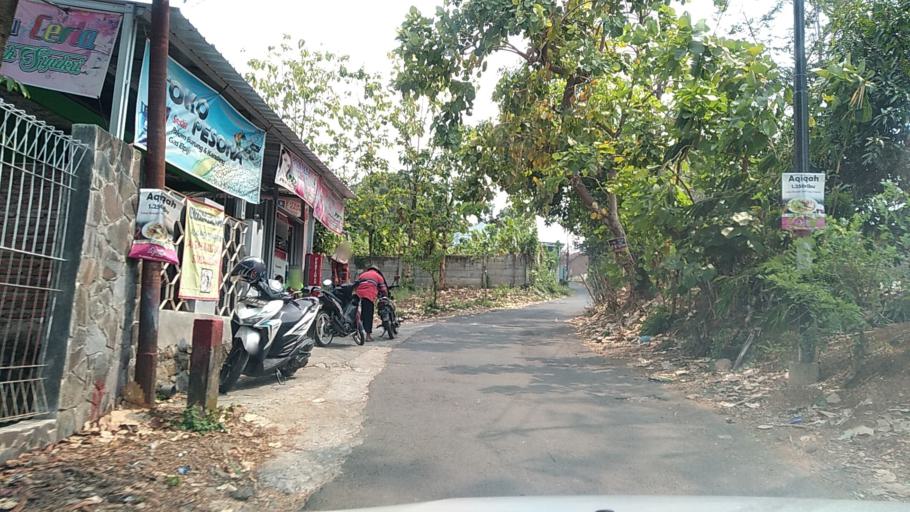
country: ID
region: Central Java
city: Semarang
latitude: -7.0041
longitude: 110.3276
